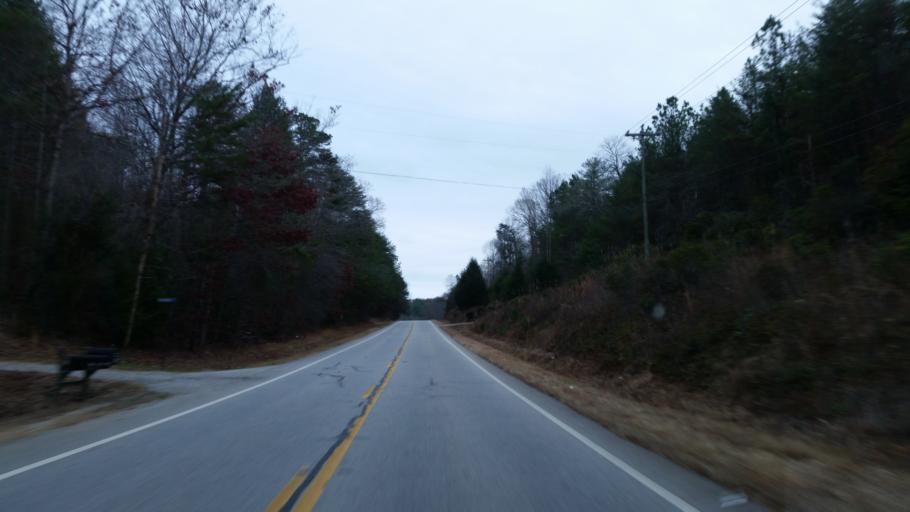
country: US
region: Georgia
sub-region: Dawson County
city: Dawsonville
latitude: 34.5186
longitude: -84.2444
